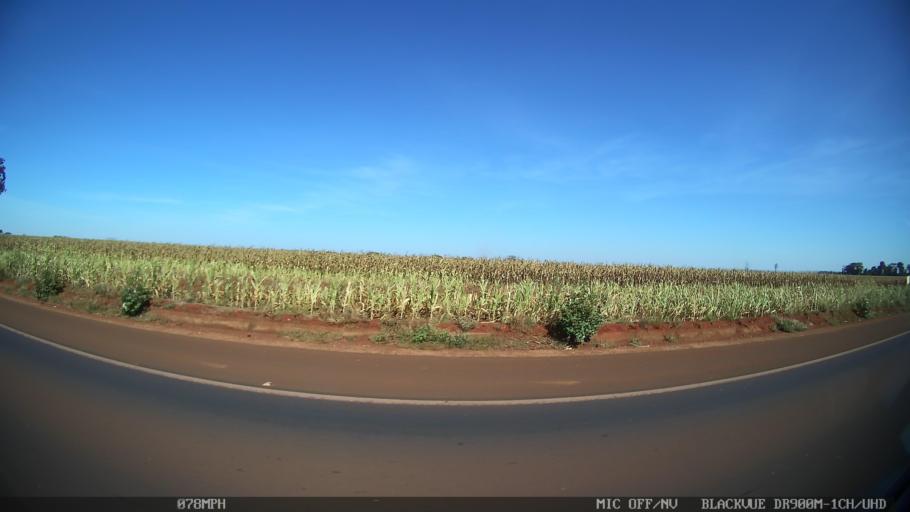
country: BR
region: Sao Paulo
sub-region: Guaira
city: Guaira
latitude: -20.4446
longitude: -48.3733
